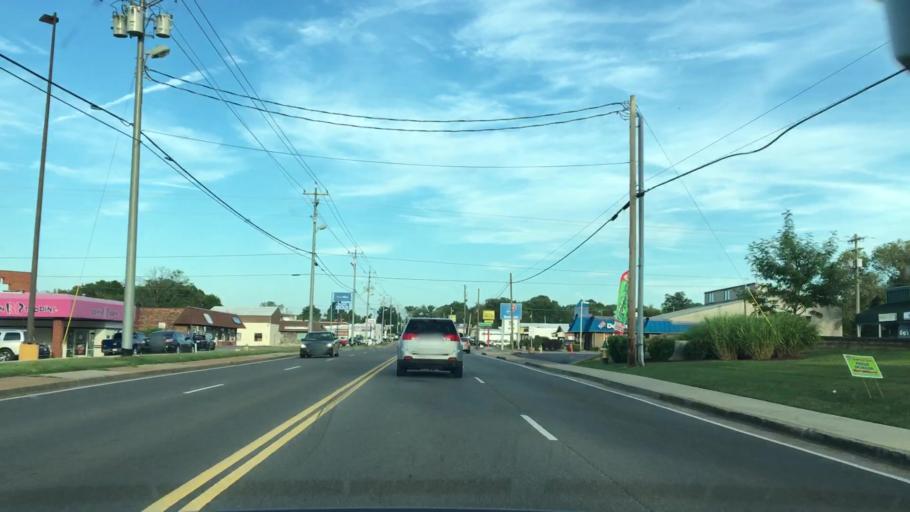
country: US
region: Tennessee
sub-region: Wilson County
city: Lebanon
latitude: 36.2117
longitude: -86.3163
